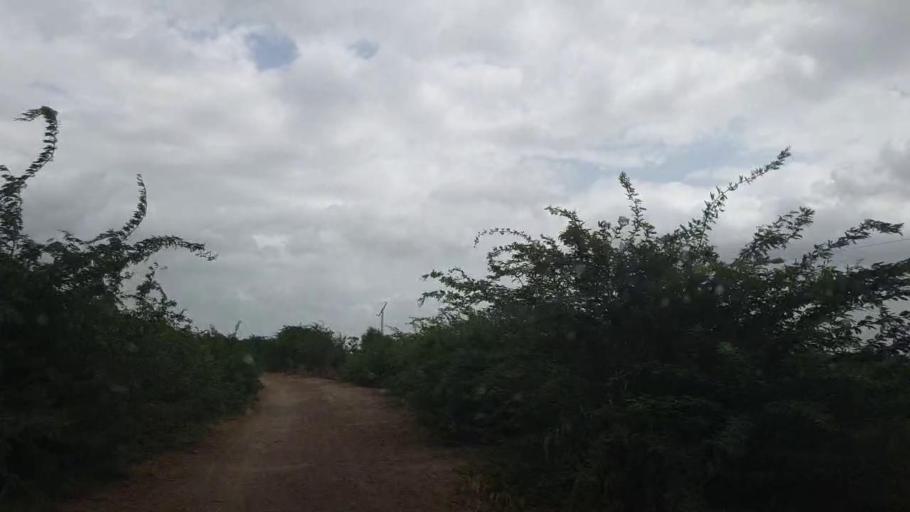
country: PK
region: Sindh
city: Badin
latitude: 24.6466
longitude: 68.9455
